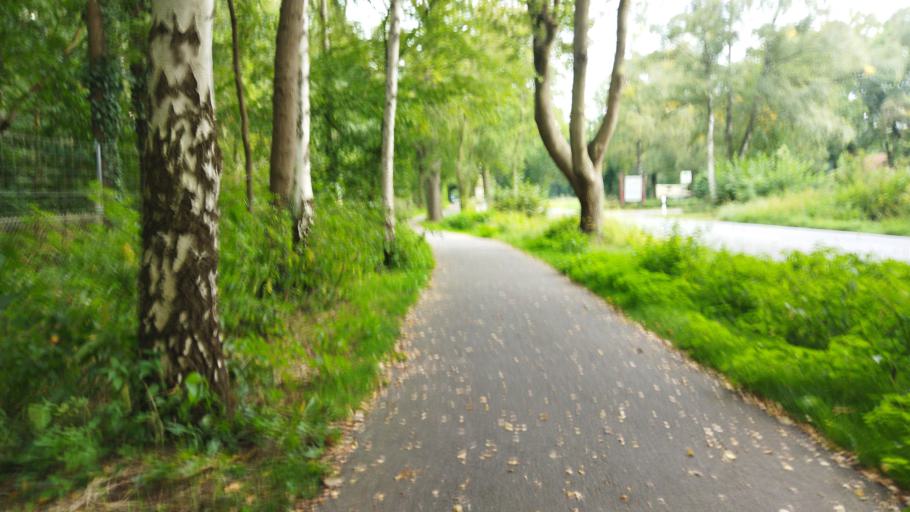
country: DE
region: North Rhine-Westphalia
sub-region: Regierungsbezirk Munster
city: Telgte
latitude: 51.9996
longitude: 7.7530
